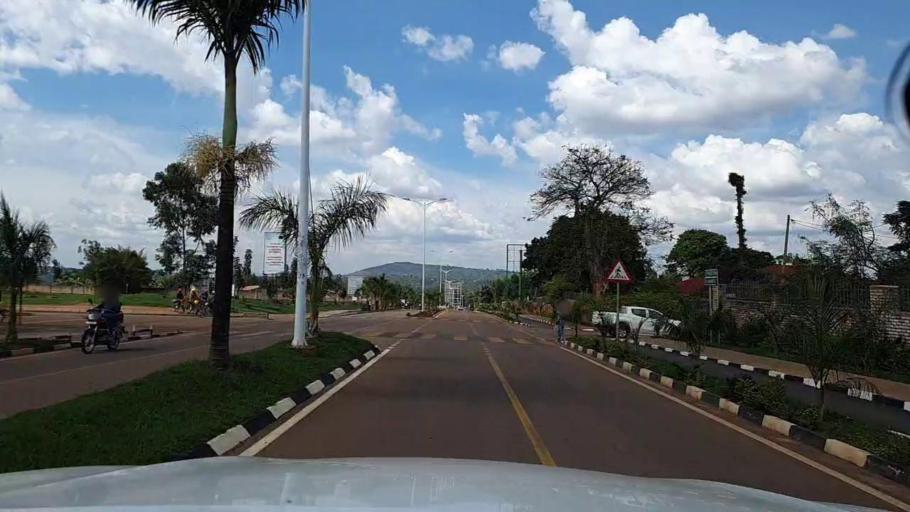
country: RW
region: Southern Province
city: Butare
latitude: -2.5958
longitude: 29.7429
